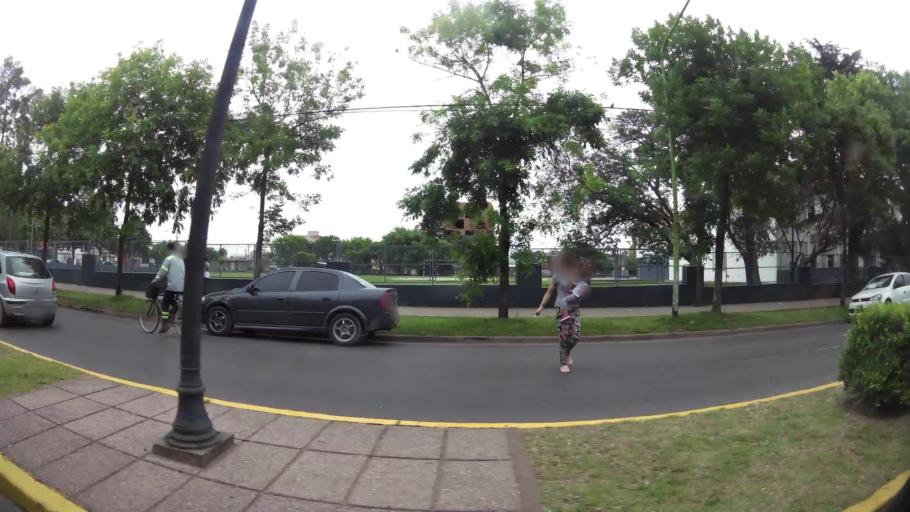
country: AR
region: Buenos Aires
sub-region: Partido de Campana
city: Campana
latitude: -34.1713
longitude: -58.9600
